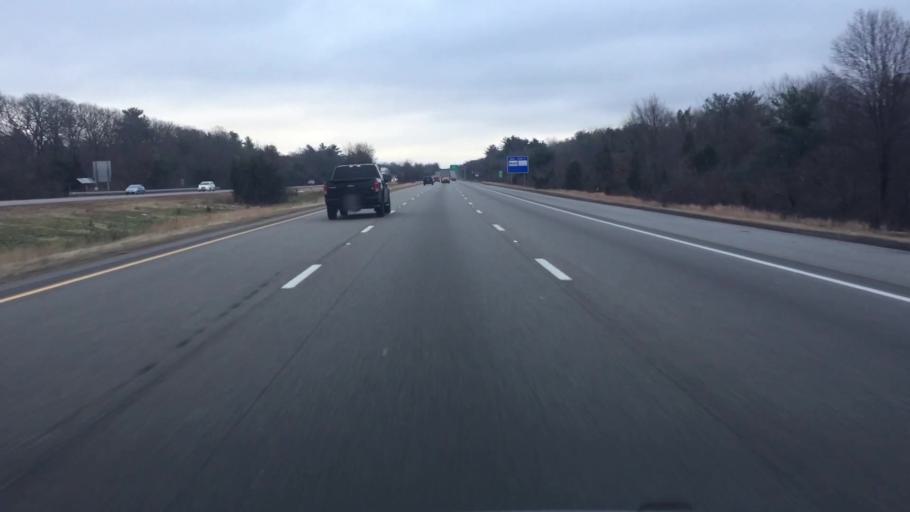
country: US
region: Massachusetts
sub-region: Bristol County
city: Mansfield Center
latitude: 42.0201
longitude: -71.2454
